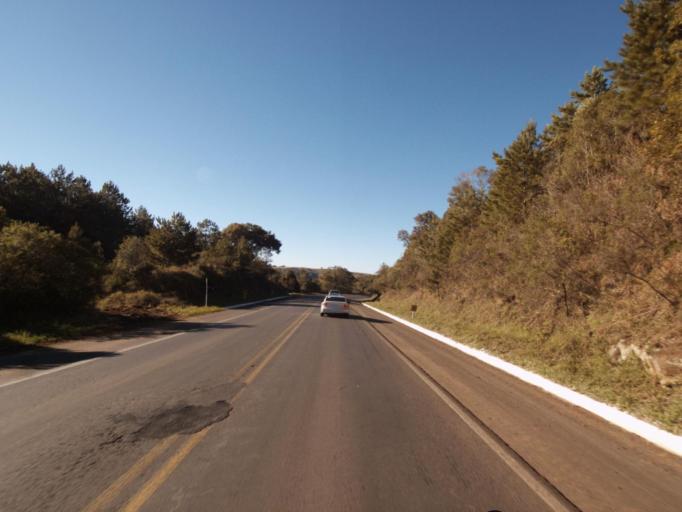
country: BR
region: Santa Catarina
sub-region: Concordia
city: Concordia
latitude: -26.9010
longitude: -51.9736
